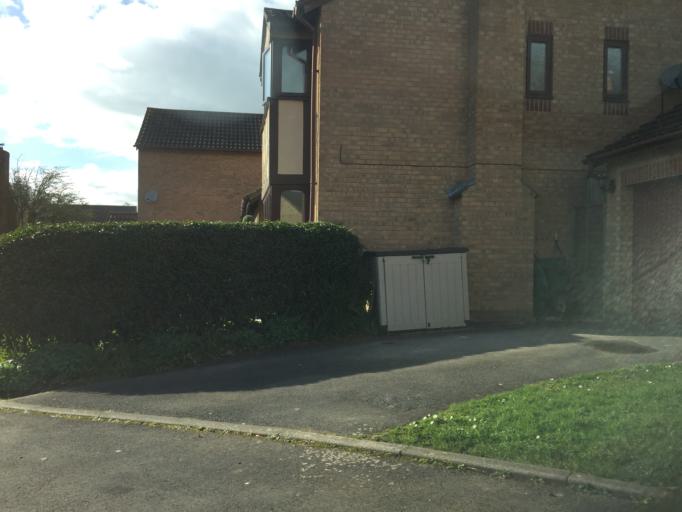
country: GB
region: England
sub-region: South Gloucestershire
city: Charfield
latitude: 51.6247
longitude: -2.4032
